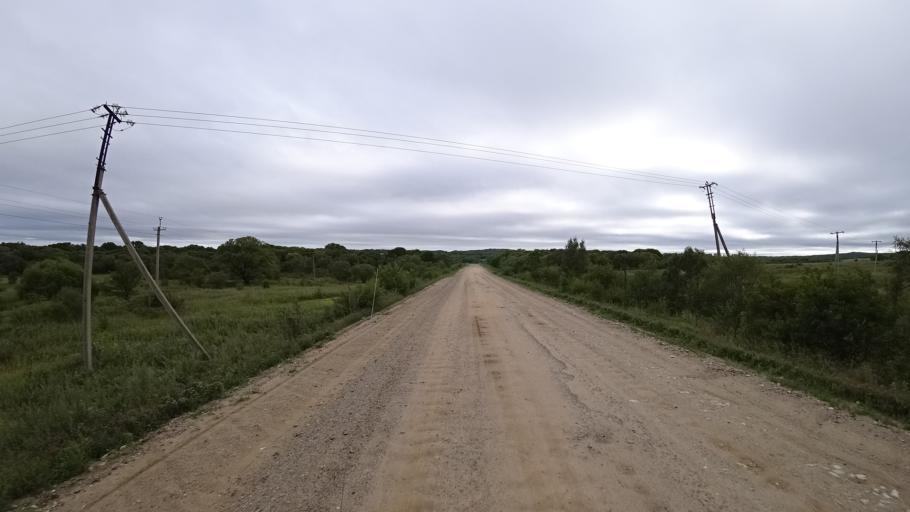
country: RU
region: Primorskiy
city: Rettikhovka
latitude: 44.1291
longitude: 132.6421
